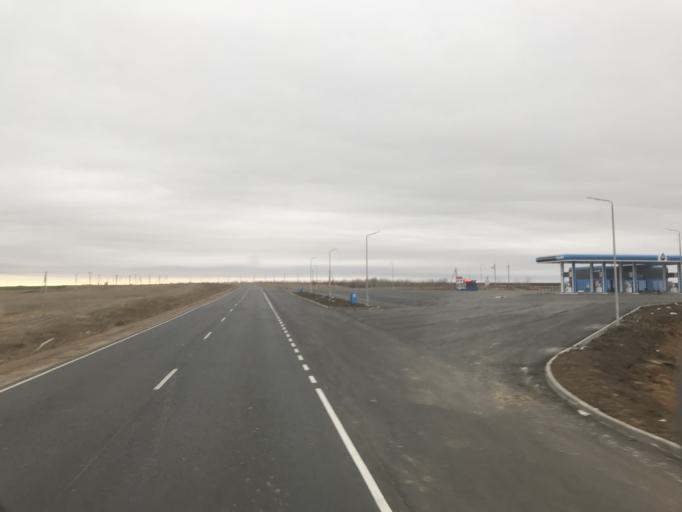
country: KZ
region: Batys Qazaqstan
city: Peremetnoe
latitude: 51.6479
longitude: 51.0121
